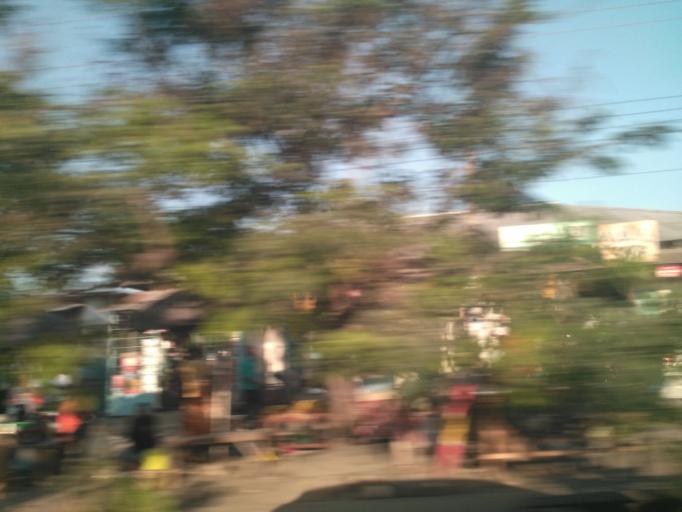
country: TZ
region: Pwani
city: Vikindu
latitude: -6.9212
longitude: 39.2709
